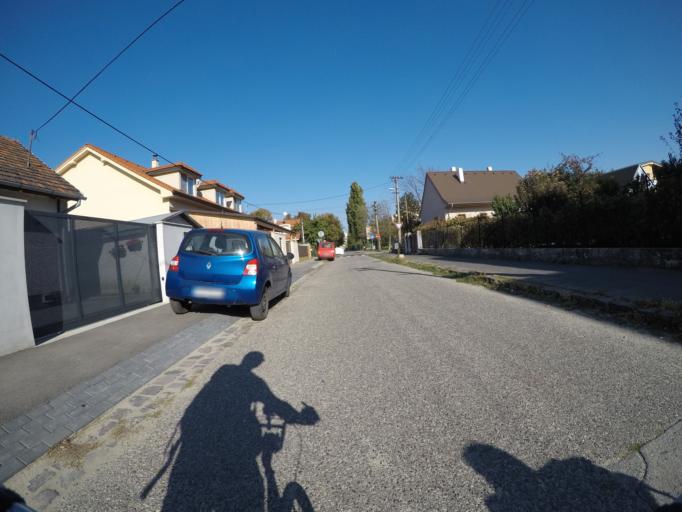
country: SK
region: Bratislavsky
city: Bratislava
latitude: 48.1703
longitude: 17.1671
